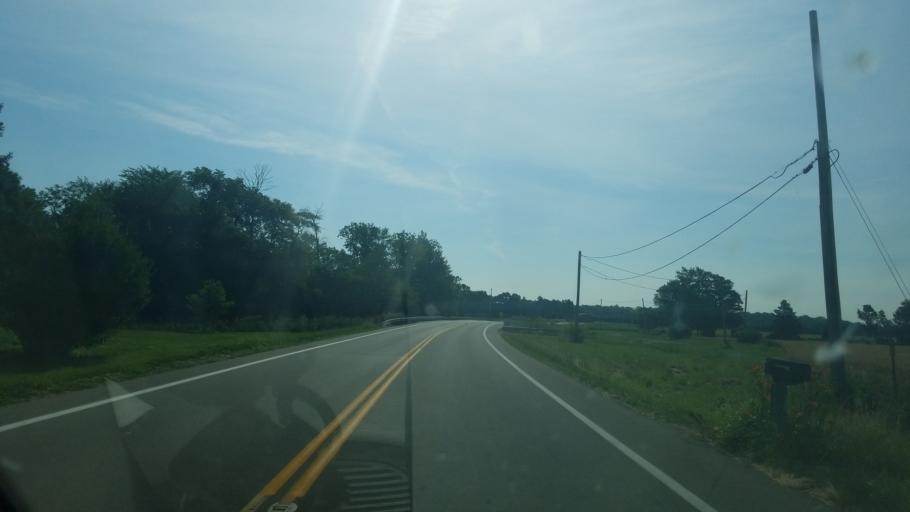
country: US
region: Ohio
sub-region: Hancock County
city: Findlay
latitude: 41.0004
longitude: -83.5907
